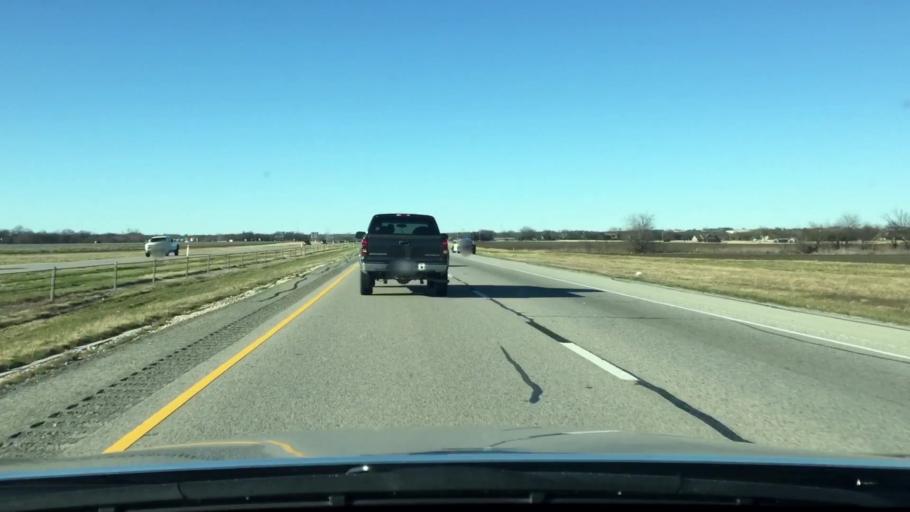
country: US
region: Texas
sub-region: Johnson County
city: Grandview
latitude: 32.2796
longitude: -97.1740
